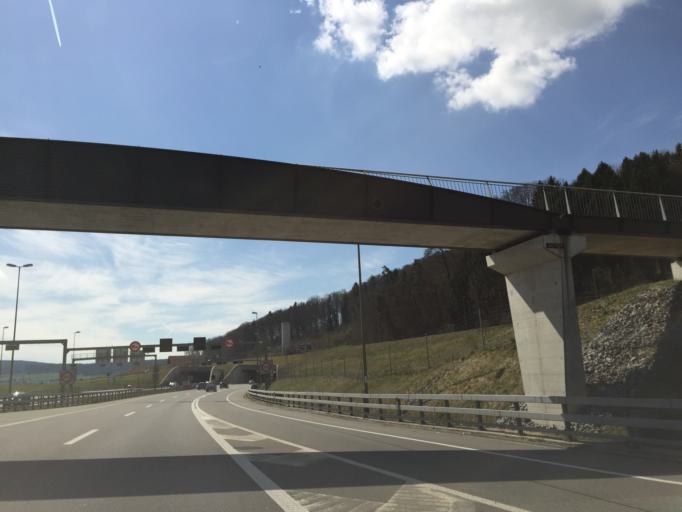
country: CH
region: Zurich
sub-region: Bezirk Affoltern
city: Wettswil / Wettswil (Dorf)
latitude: 47.3373
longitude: 8.4598
